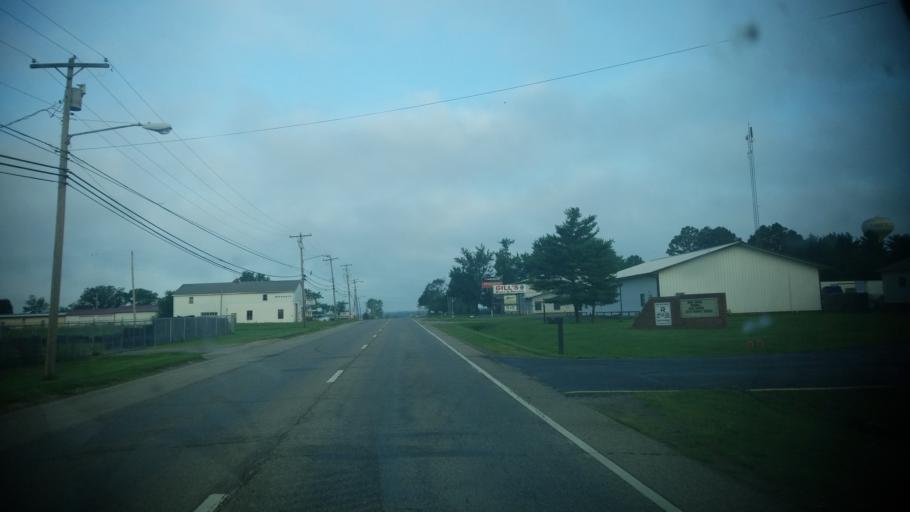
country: US
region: Illinois
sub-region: Wayne County
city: Fairfield
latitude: 38.3797
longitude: -88.3841
